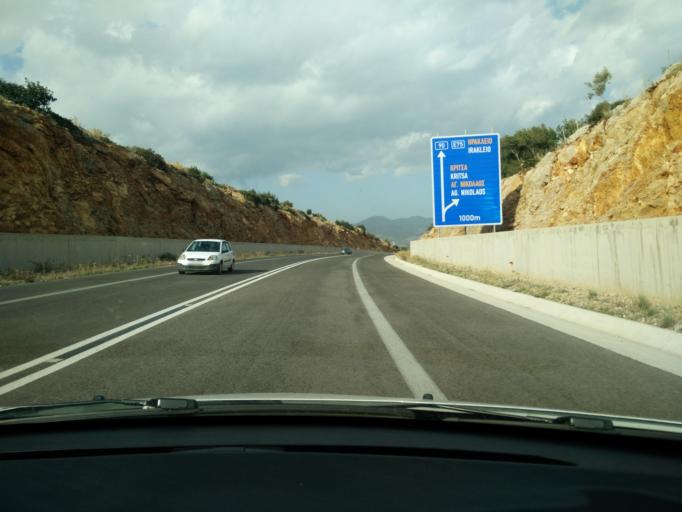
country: GR
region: Crete
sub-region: Nomos Lasithiou
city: Agios Nikolaos
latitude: 35.1727
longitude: 25.7011
